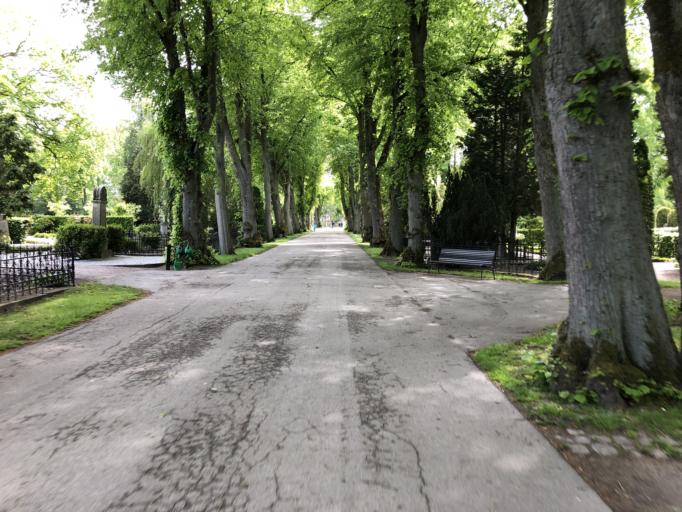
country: SE
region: Skane
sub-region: Lunds Kommun
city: Lund
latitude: 55.7141
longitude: 13.1942
